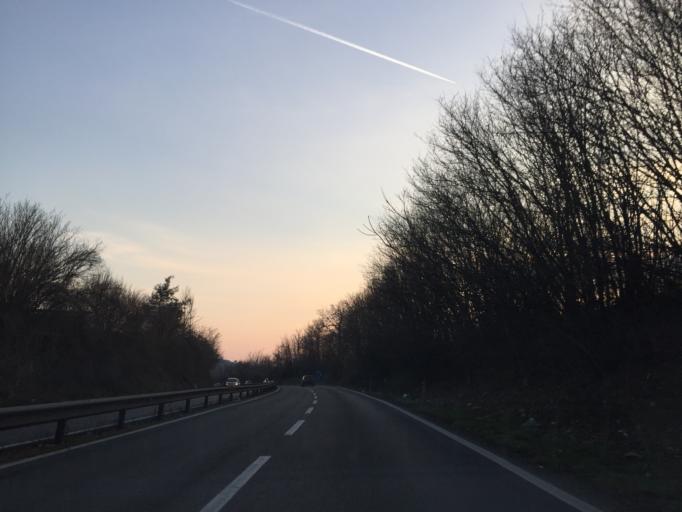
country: IT
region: Campania
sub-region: Provincia di Avellino
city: Atripalda
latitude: 40.9248
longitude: 14.8273
